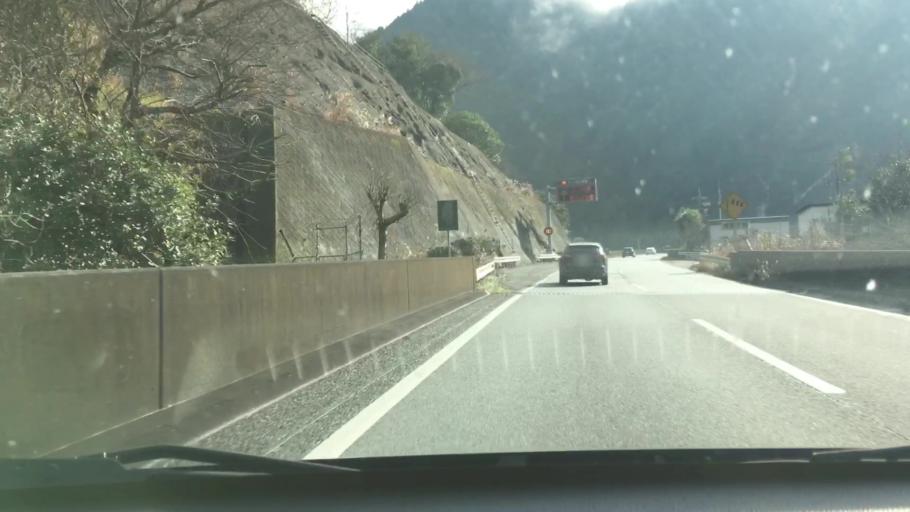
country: JP
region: Kumamoto
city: Yatsushiro
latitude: 32.4271
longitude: 130.7025
